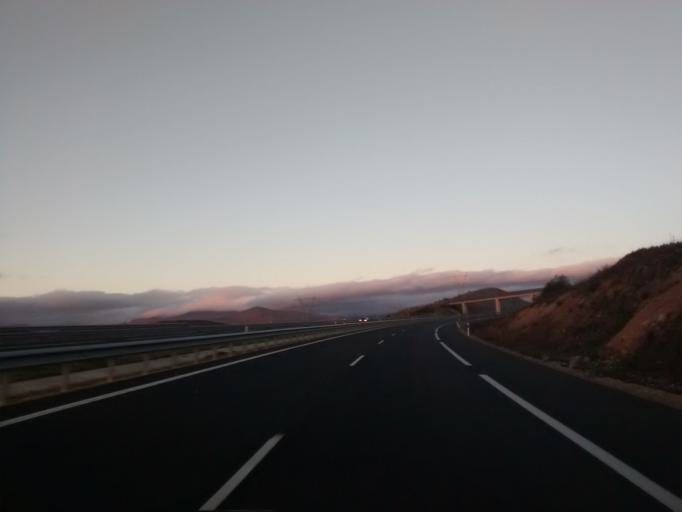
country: ES
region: Castille and Leon
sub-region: Provincia de Palencia
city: Aguilar de Campoo
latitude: 42.7965
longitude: -4.2369
